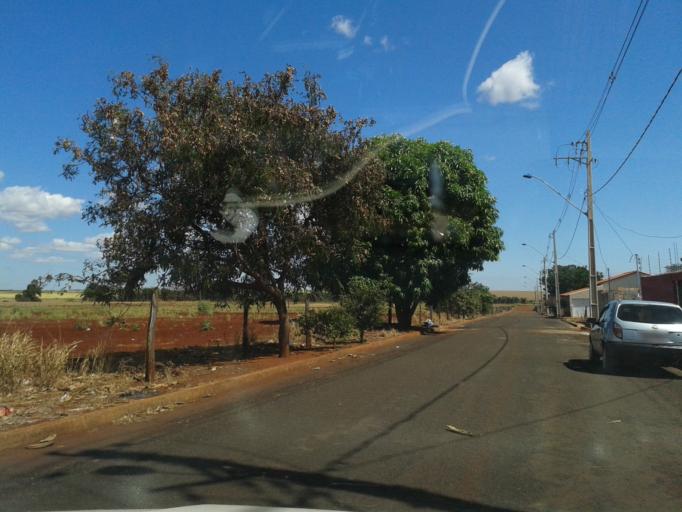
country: BR
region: Minas Gerais
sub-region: Centralina
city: Centralina
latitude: -18.5947
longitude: -49.1998
